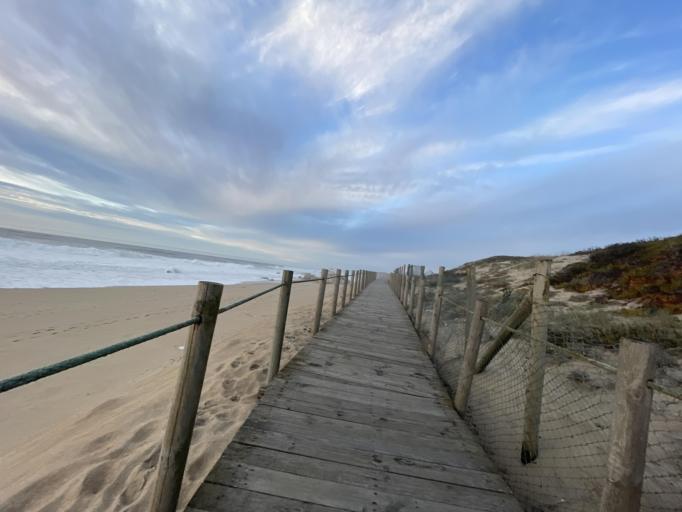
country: PT
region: Porto
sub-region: Vila Nova de Gaia
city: Arcozelo
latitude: 41.0628
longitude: -8.6569
